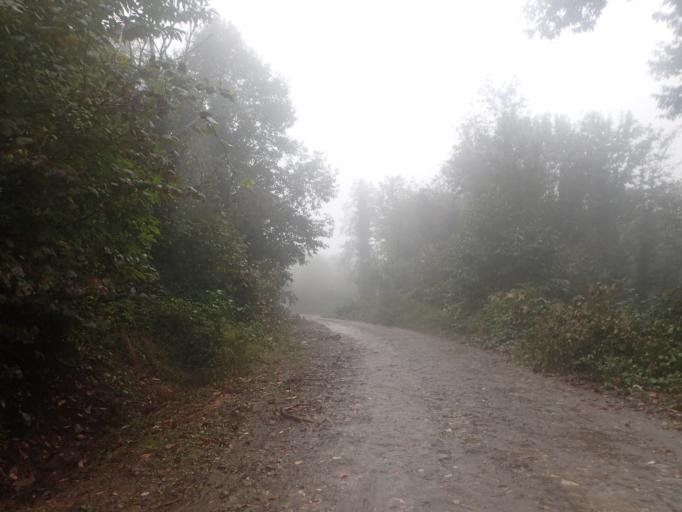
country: TR
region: Ordu
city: Persembe
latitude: 41.0284
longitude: 37.7138
